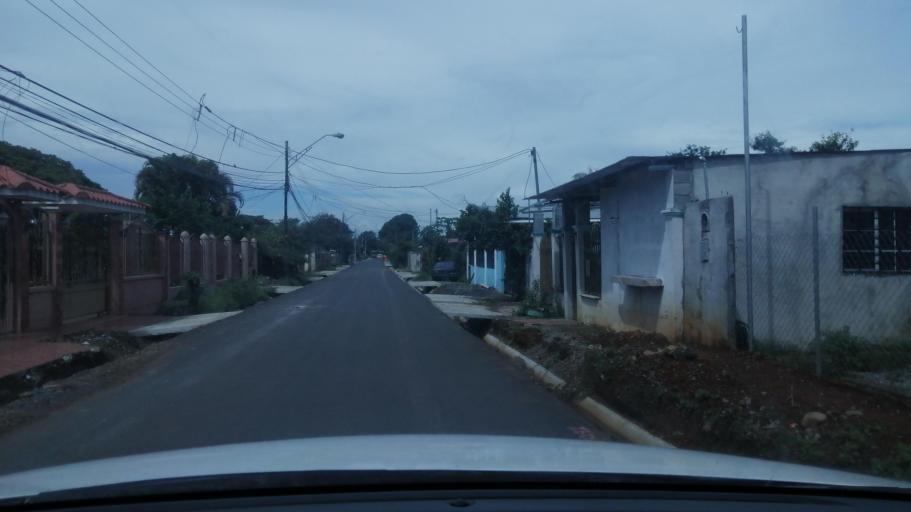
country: PA
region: Chiriqui
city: David
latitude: 8.4178
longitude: -82.4484
